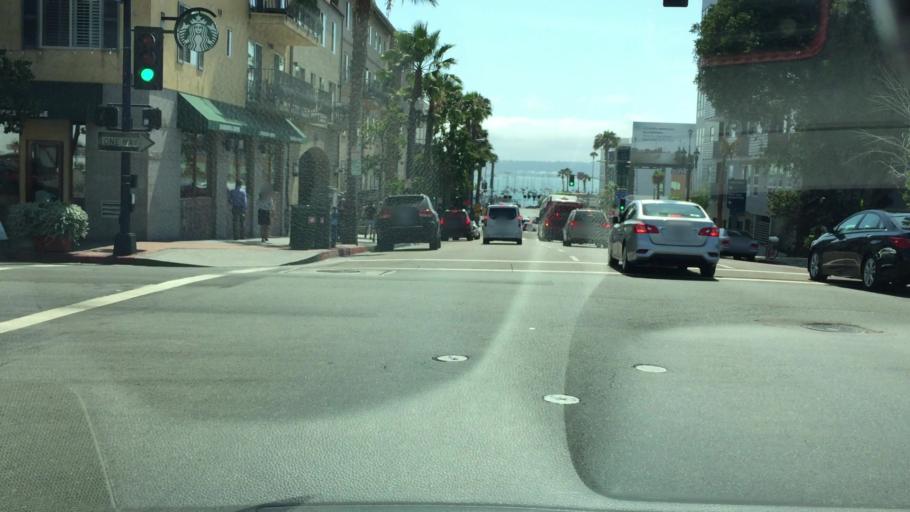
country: US
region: California
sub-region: San Diego County
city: San Diego
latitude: 32.7264
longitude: -117.1694
